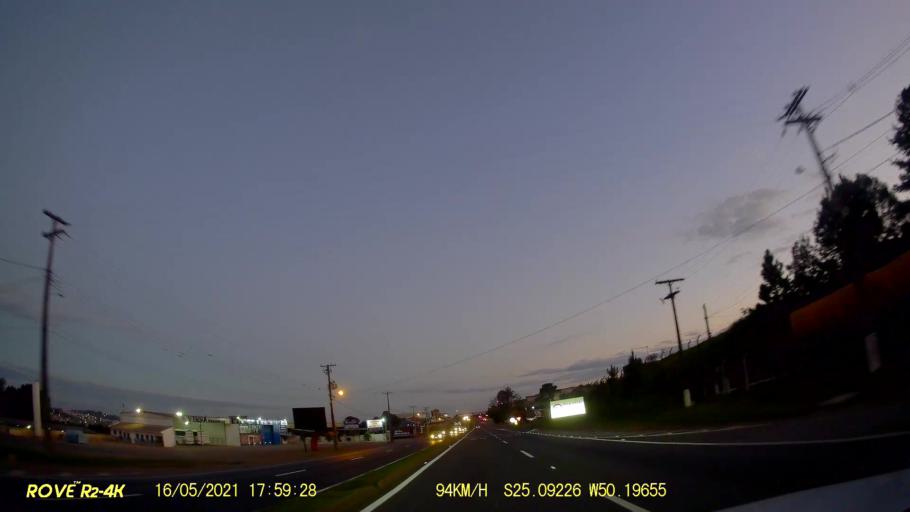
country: BR
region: Parana
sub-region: Ponta Grossa
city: Ponta Grossa
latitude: -25.0920
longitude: -50.1965
